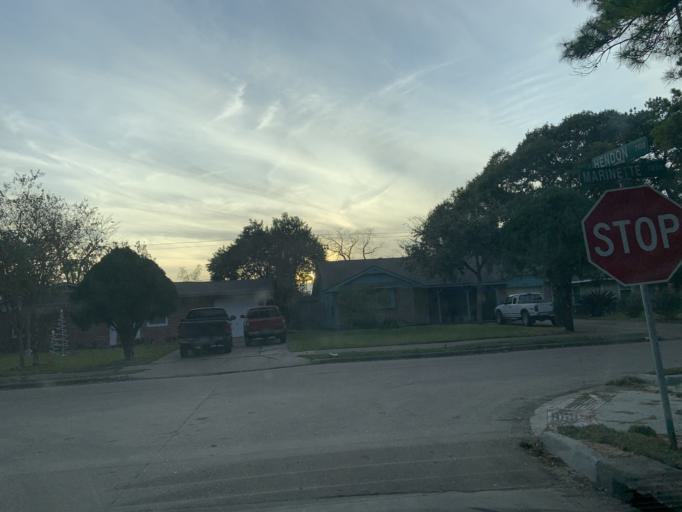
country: US
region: Texas
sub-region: Harris County
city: Bellaire
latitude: 29.6953
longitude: -95.5105
